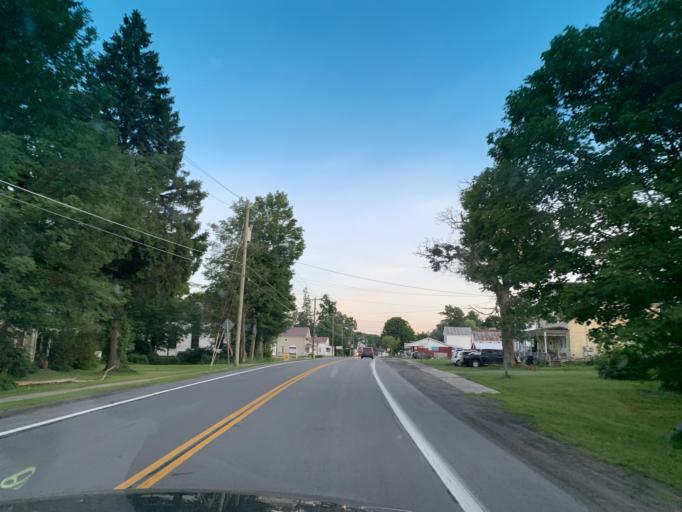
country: US
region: New York
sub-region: Oneida County
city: Waterville
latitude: 42.8826
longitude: -75.2507
